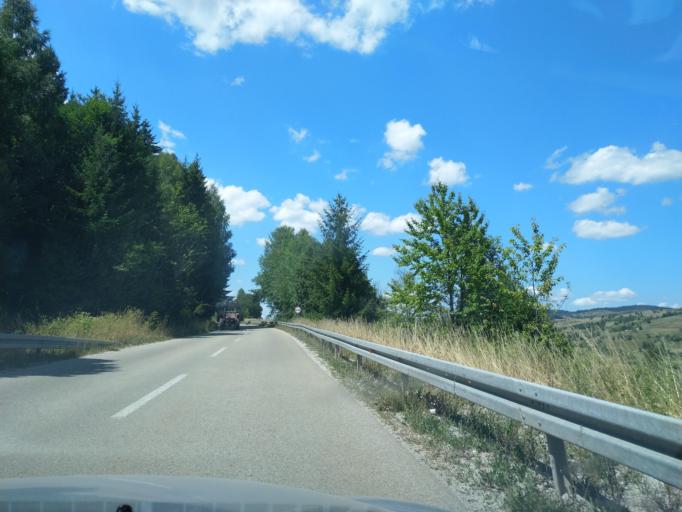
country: RS
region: Central Serbia
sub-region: Zlatiborski Okrug
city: Nova Varos
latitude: 43.3282
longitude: 19.8573
